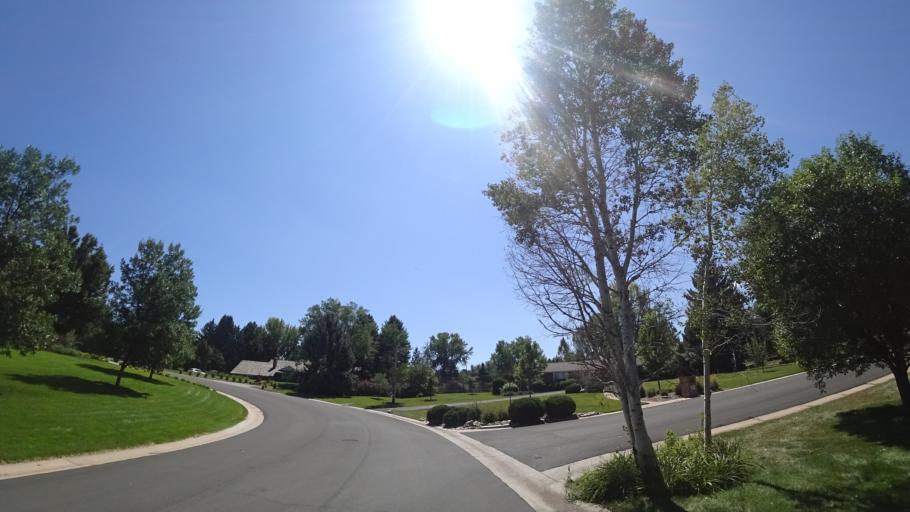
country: US
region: Colorado
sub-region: Arapahoe County
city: Cherry Hills Village
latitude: 39.6325
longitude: -104.9560
